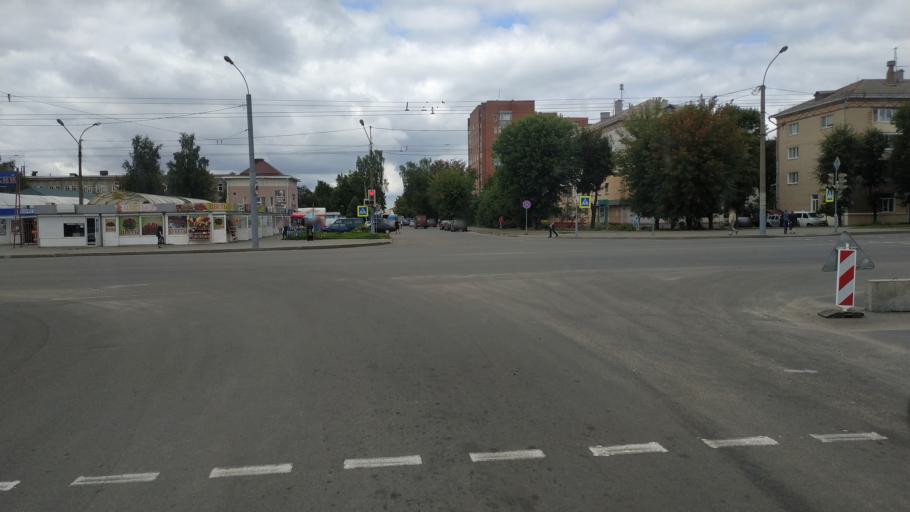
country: BY
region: Mogilev
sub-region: Mahilyowski Rayon
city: Veyno
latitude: 53.8824
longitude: 30.4076
